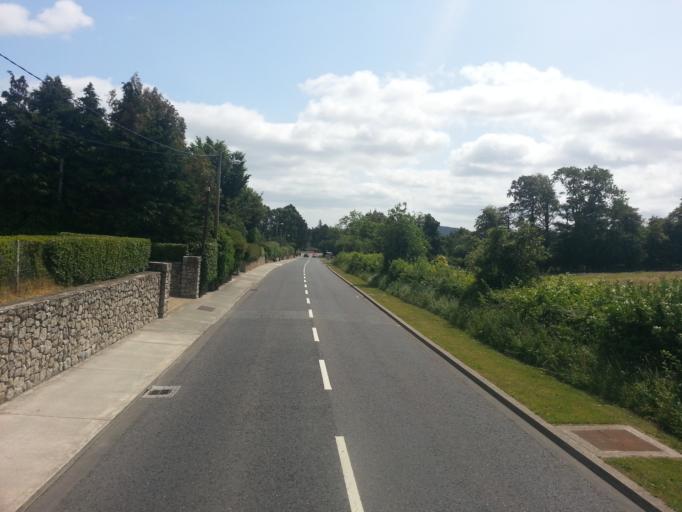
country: IE
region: Leinster
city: Sandyford
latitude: 53.2506
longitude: -6.2101
